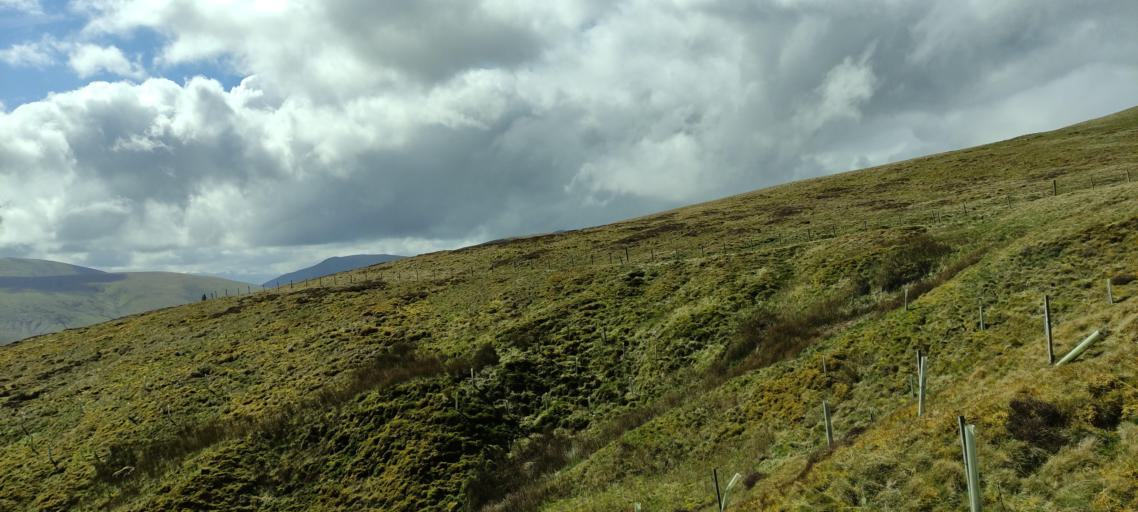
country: GB
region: England
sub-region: Cumbria
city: Keswick
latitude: 54.6972
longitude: -3.0532
